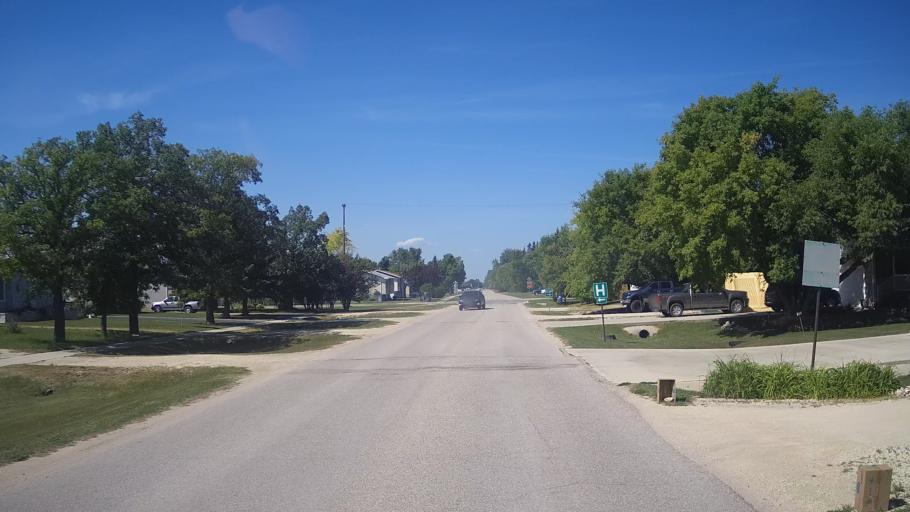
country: CA
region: Manitoba
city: Stonewall
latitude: 50.1292
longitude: -97.3334
